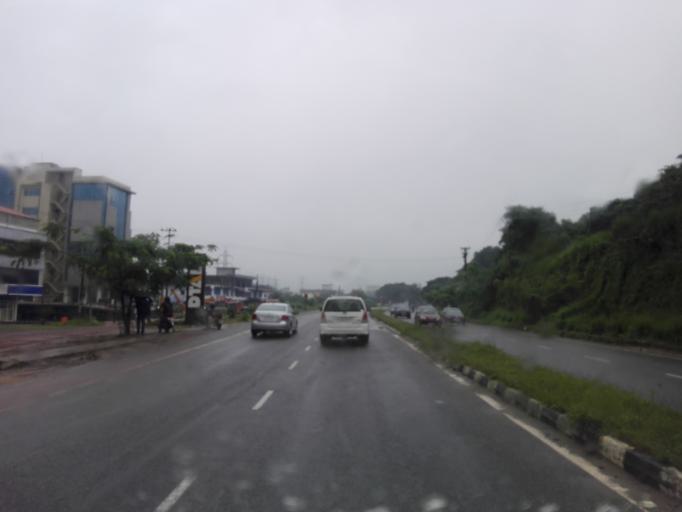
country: IN
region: Kerala
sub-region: Ernakulam
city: Elur
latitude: 10.0436
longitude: 76.3382
